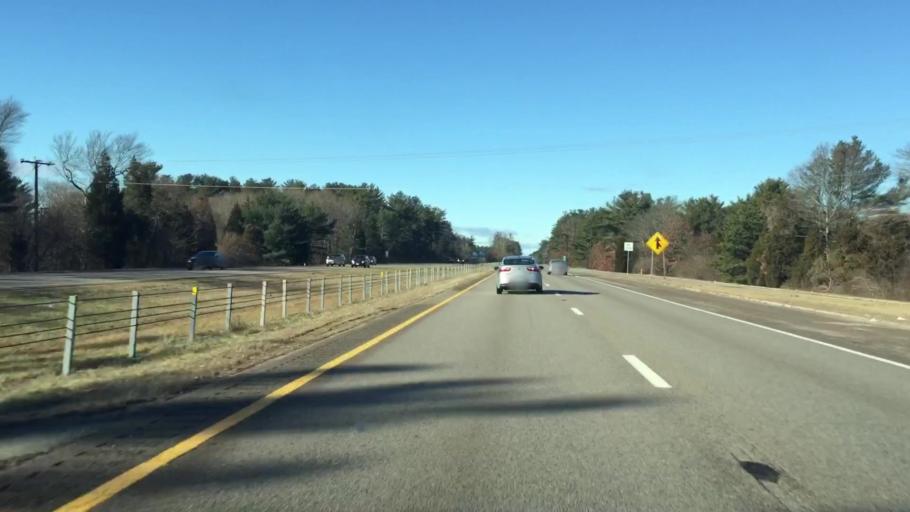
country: US
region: Massachusetts
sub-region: Plymouth County
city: Middleborough Center
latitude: 41.9041
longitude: -70.9667
